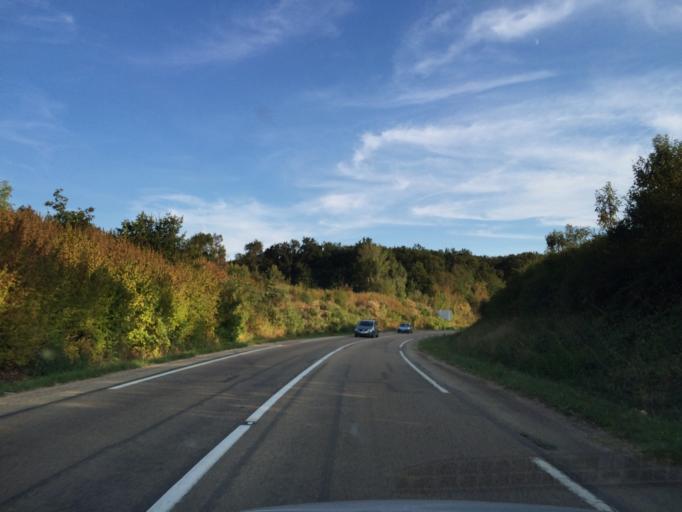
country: FR
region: Bourgogne
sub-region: Departement de l'Yonne
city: Moneteau
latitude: 47.8384
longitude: 3.5551
